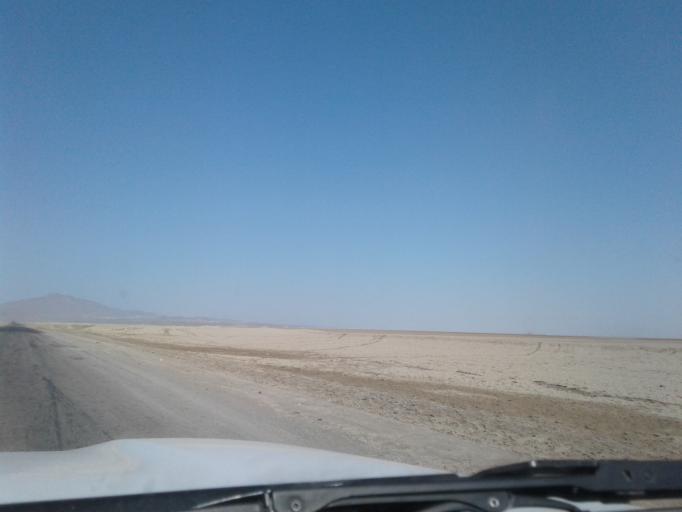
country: TM
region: Balkan
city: Gumdag
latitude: 39.2147
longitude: 54.6431
